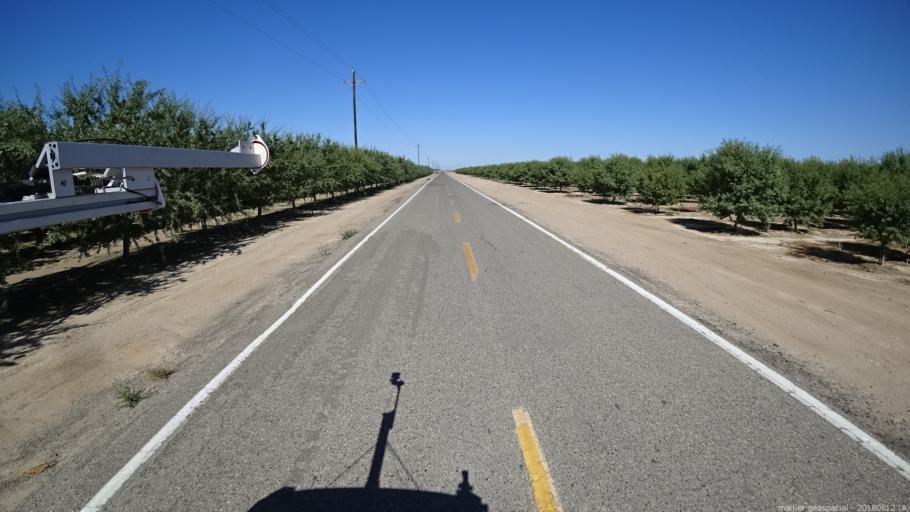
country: US
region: California
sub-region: Fresno County
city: Firebaugh
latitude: 37.0182
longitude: -120.4239
